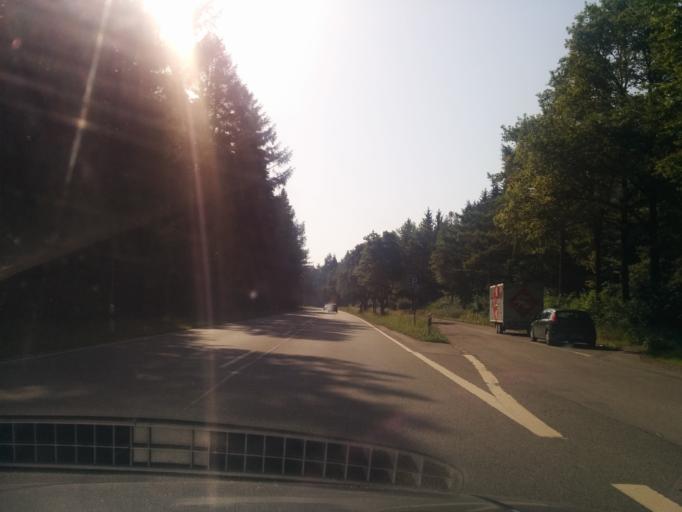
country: DE
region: Bavaria
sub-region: Upper Bavaria
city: Grunwald
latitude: 48.0351
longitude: 11.5457
